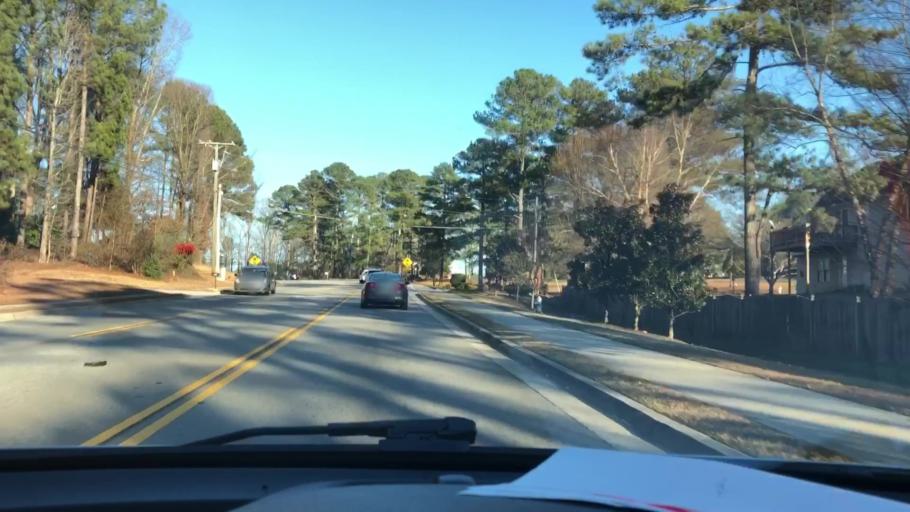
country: US
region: Georgia
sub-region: Gwinnett County
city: Snellville
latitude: 33.9026
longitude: -84.0443
